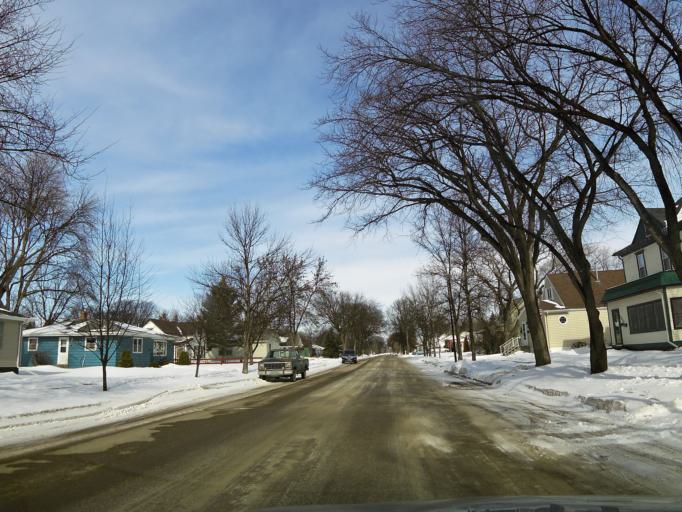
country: US
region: North Dakota
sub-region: Walsh County
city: Grafton
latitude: 48.4137
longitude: -97.4173
